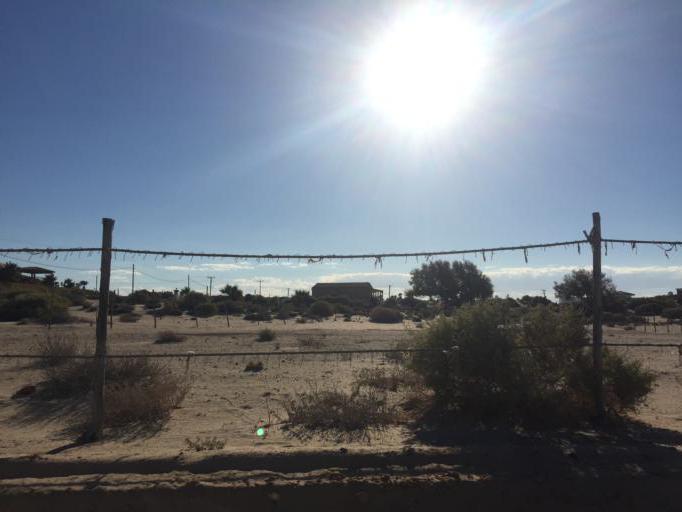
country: MX
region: Sonora
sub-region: Puerto Penasco
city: Puerto Penasco
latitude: 31.2874
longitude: -113.4761
